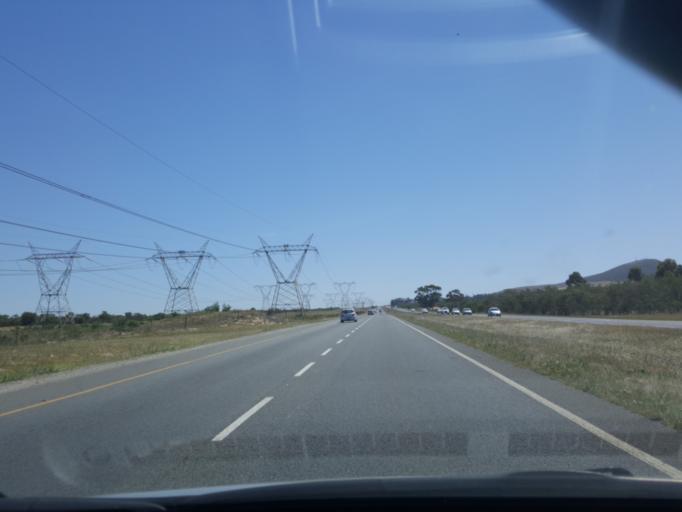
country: ZA
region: Western Cape
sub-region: City of Cape Town
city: Sunset Beach
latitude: -33.7492
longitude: 18.5463
